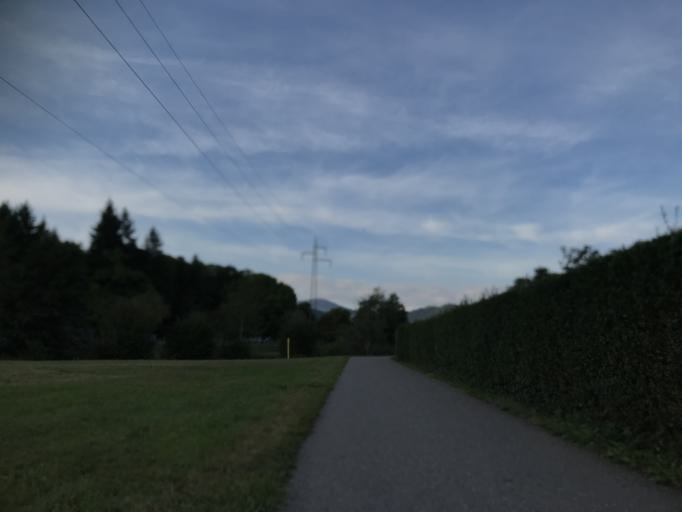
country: DE
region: Baden-Wuerttemberg
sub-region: Freiburg Region
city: Schopfheim
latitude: 47.6615
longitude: 7.8310
